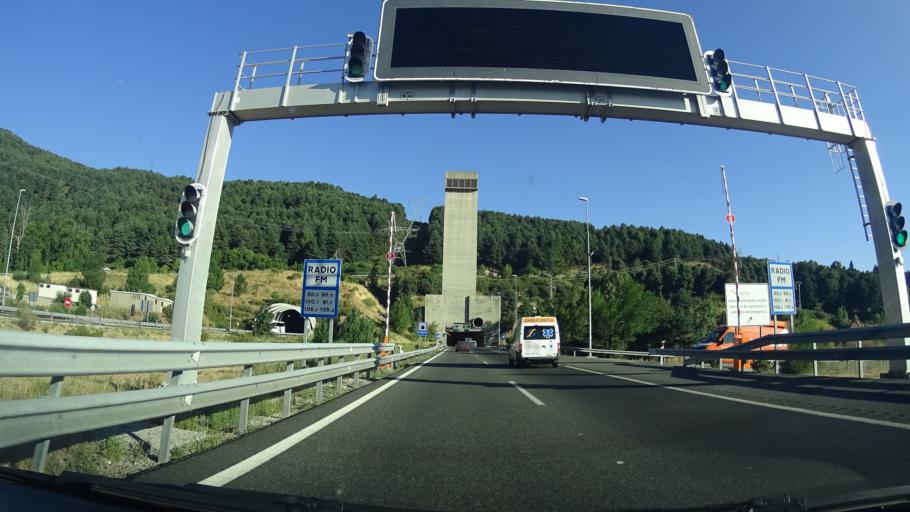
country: ES
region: Madrid
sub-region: Provincia de Madrid
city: Guadarrama
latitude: 40.6989
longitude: -4.1283
